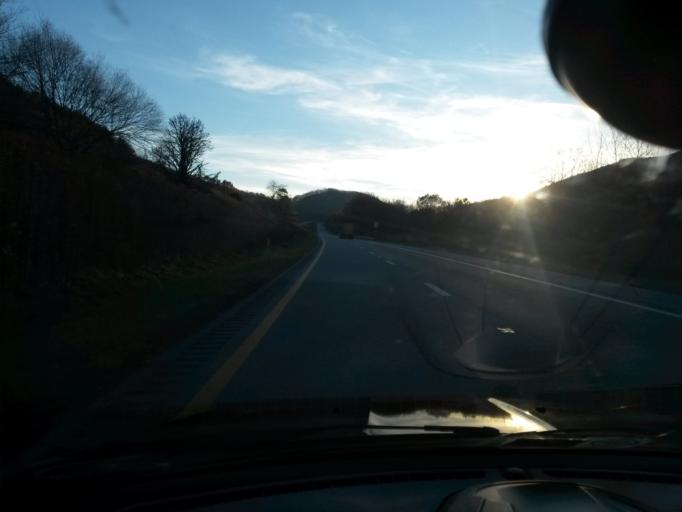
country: US
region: Virginia
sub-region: City of Lexington
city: Lexington
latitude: 37.8837
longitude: -79.6018
